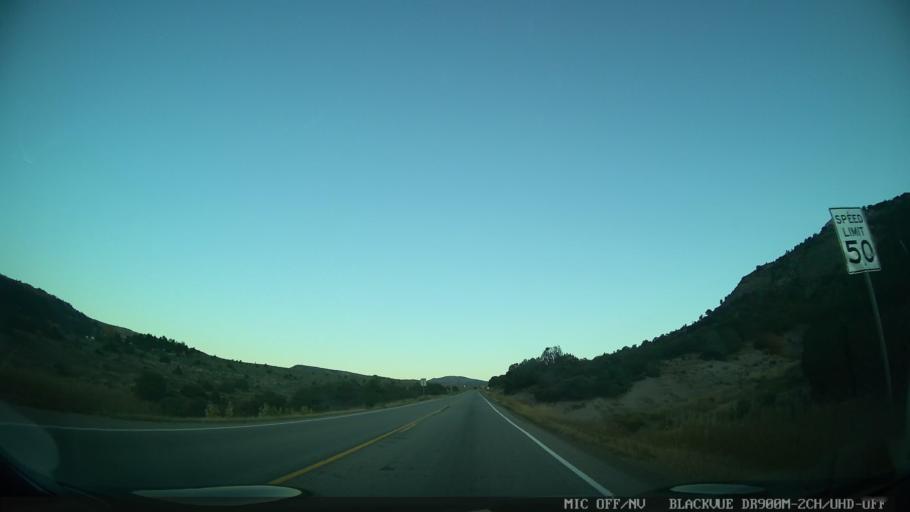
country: US
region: Colorado
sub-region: Eagle County
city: Edwards
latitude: 39.7045
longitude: -106.6804
